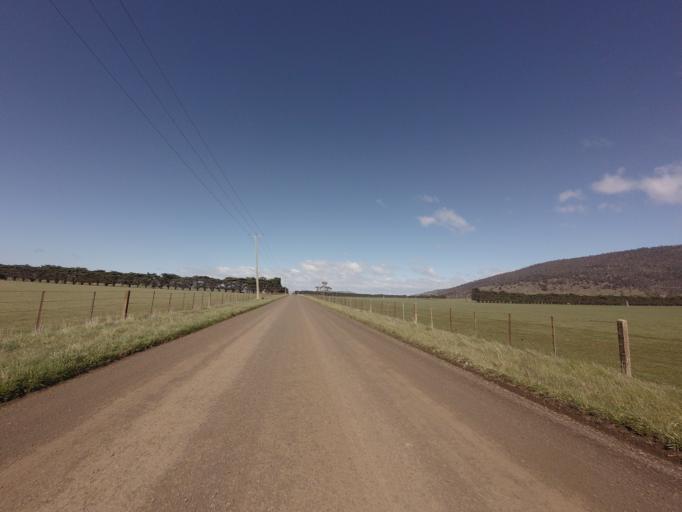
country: AU
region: Tasmania
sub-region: Northern Midlands
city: Evandale
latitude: -41.9600
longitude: 147.4381
